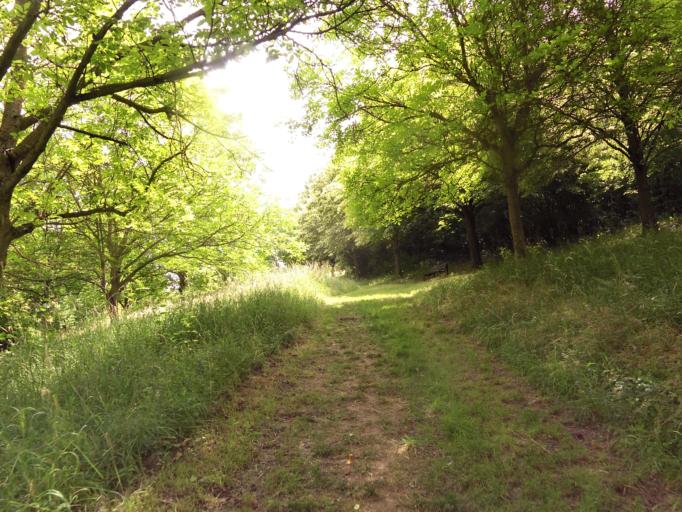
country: DE
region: Bavaria
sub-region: Regierungsbezirk Unterfranken
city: Wuerzburg
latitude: 49.7950
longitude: 9.9761
